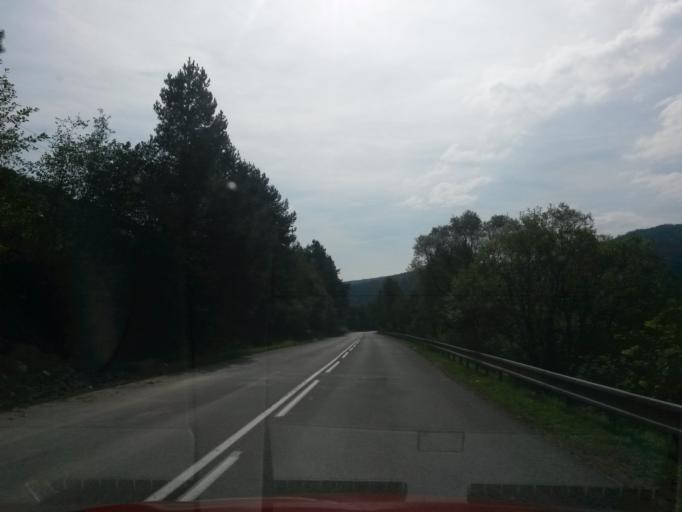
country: SK
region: Kosicky
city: Gelnica
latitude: 48.8277
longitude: 20.8835
